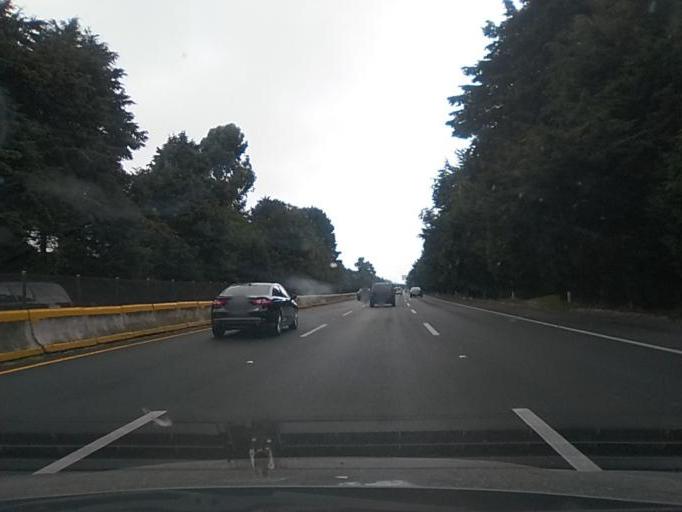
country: MX
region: Morelos
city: Tres Marias
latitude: 19.1256
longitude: -99.1765
